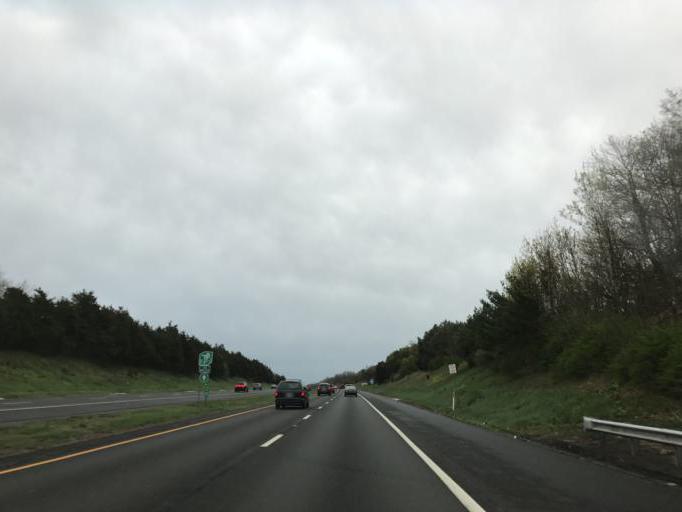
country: US
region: New Jersey
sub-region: Somerset County
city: Bridgewater
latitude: 40.6264
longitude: -74.6417
